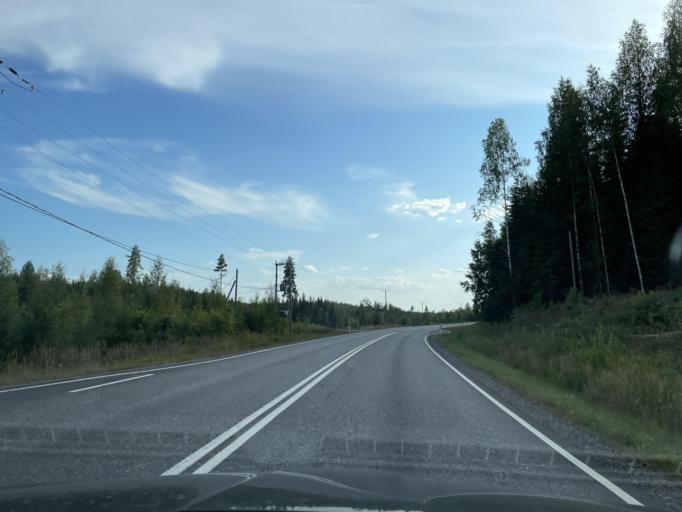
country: FI
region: Paijanne Tavastia
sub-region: Lahti
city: Auttoinen
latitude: 61.3226
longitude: 25.1639
